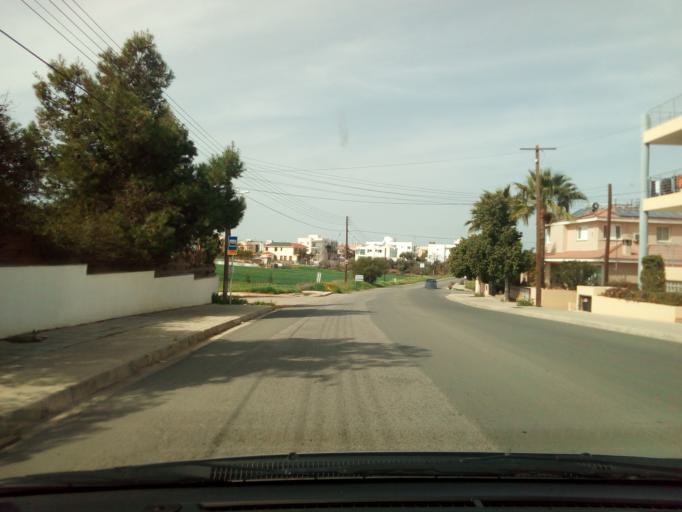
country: CY
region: Lefkosia
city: Tseri
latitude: 35.0995
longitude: 33.3121
